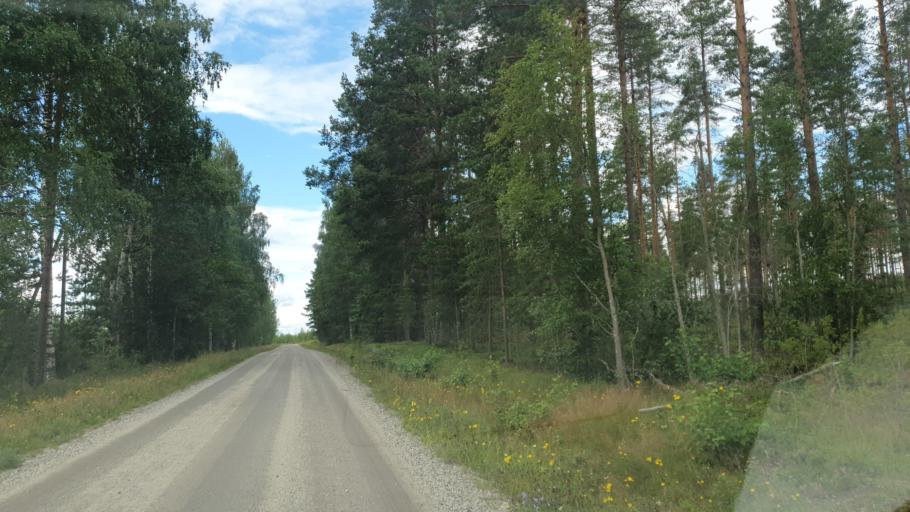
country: FI
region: Kainuu
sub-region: Kehys-Kainuu
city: Kuhmo
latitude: 64.1097
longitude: 29.3815
